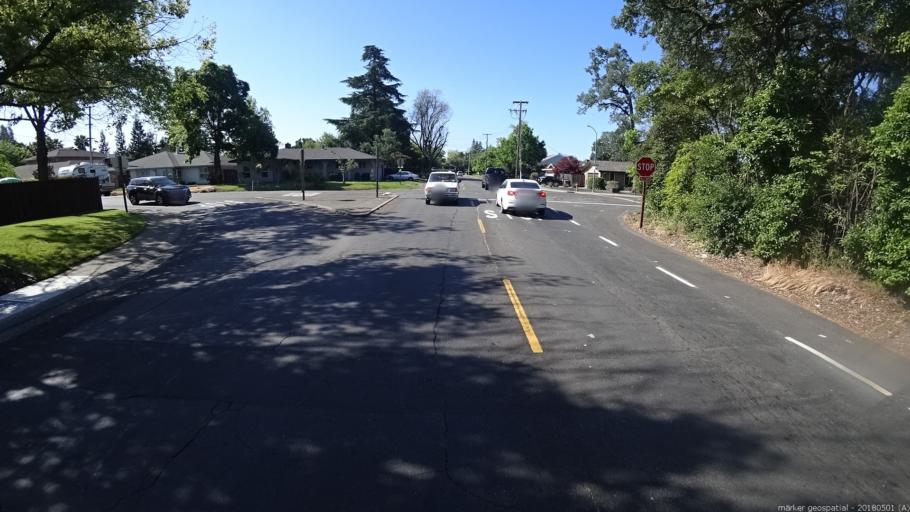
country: US
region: California
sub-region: Sacramento County
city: Arden-Arcade
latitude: 38.6342
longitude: -121.3675
